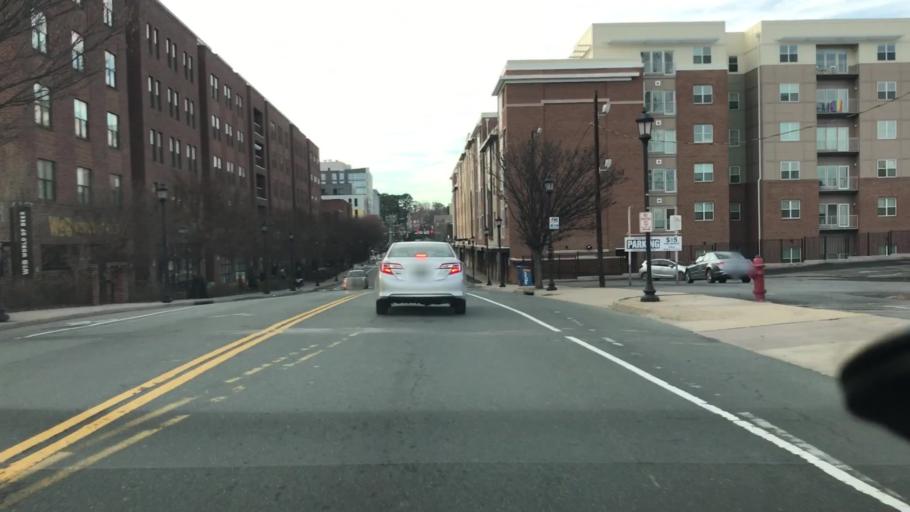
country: US
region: Virginia
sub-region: City of Charlottesville
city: Charlottesville
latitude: 38.0321
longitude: -78.4922
